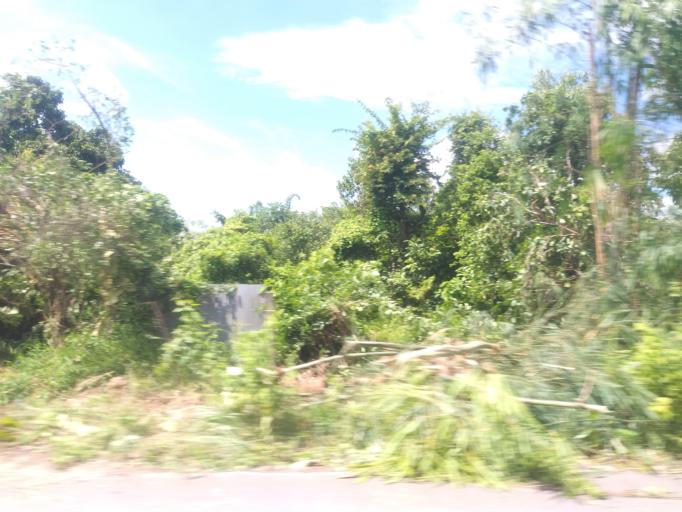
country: TH
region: Nakhon Nayok
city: Nakhon Nayok
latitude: 14.2749
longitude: 101.2776
